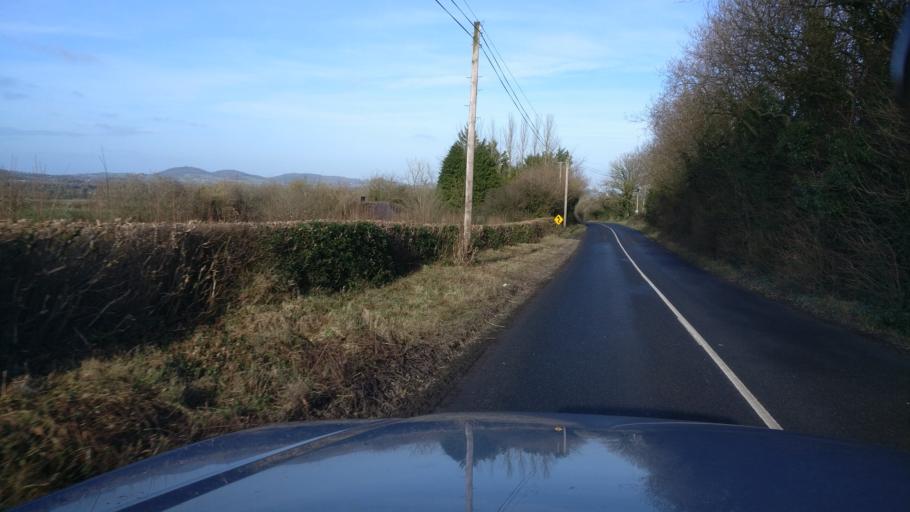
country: IE
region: Leinster
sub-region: Laois
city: Stradbally
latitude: 52.9492
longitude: -7.1990
